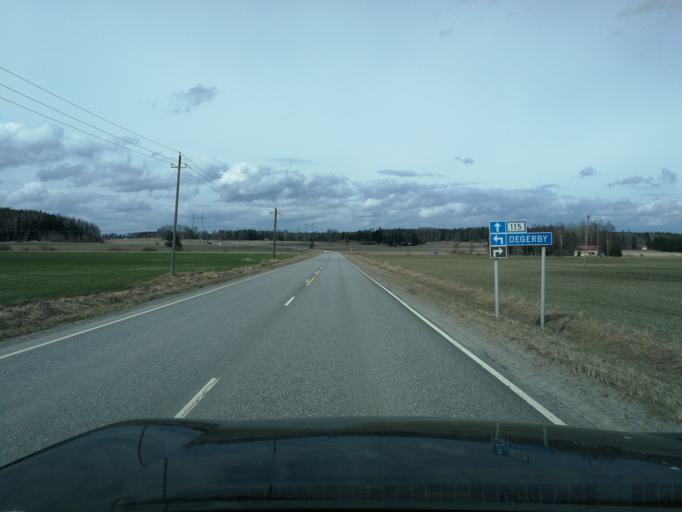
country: FI
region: Uusimaa
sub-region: Helsinki
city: Siuntio
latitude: 60.1140
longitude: 24.2411
